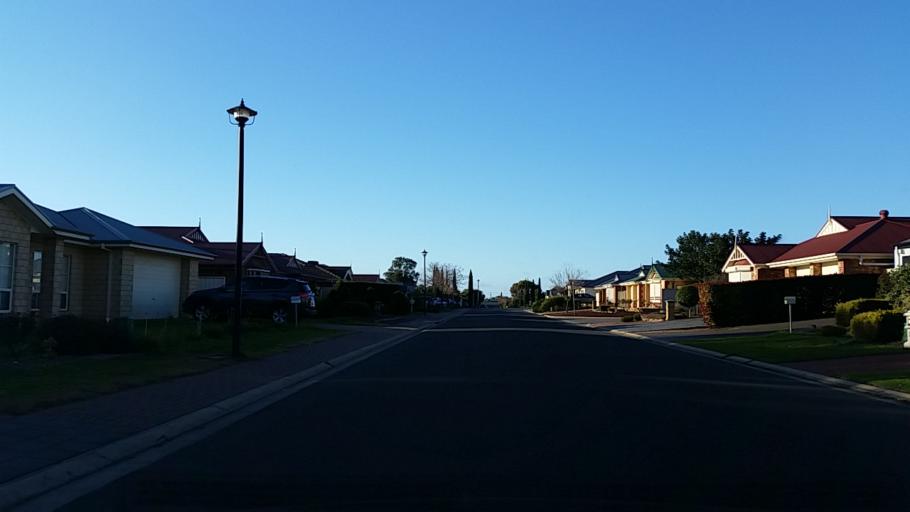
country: AU
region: South Australia
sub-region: Playford
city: Smithfield
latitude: -34.6836
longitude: 138.6810
